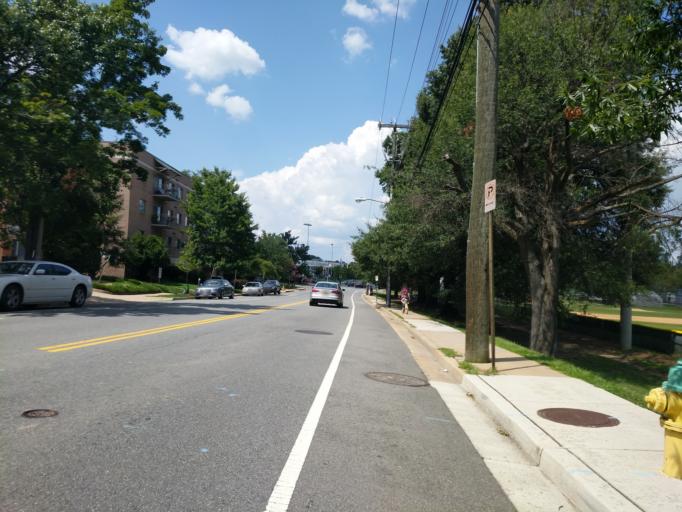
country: US
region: Virginia
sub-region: Arlington County
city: Arlington
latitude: 38.8845
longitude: -77.1080
